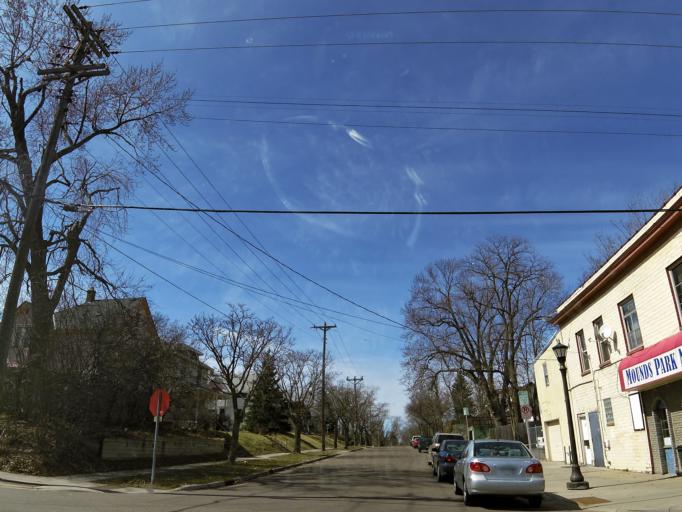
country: US
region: Minnesota
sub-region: Ramsey County
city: Saint Paul
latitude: 44.9488
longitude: -93.0557
